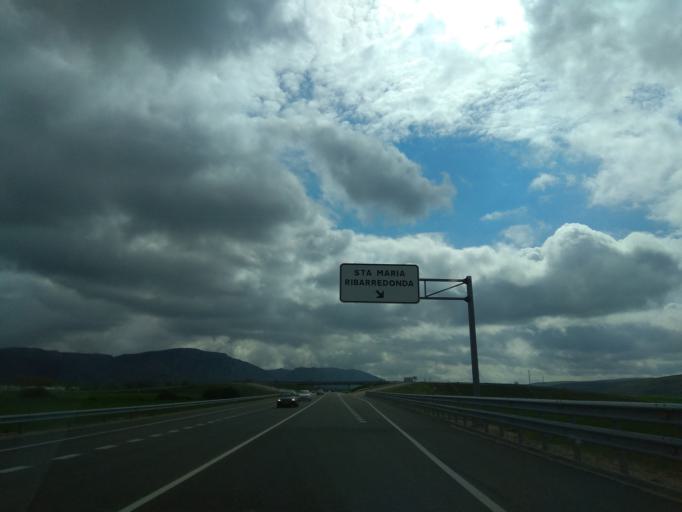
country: ES
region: Castille and Leon
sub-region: Provincia de Burgos
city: Villanueva de Teba
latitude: 42.6362
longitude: -3.1758
